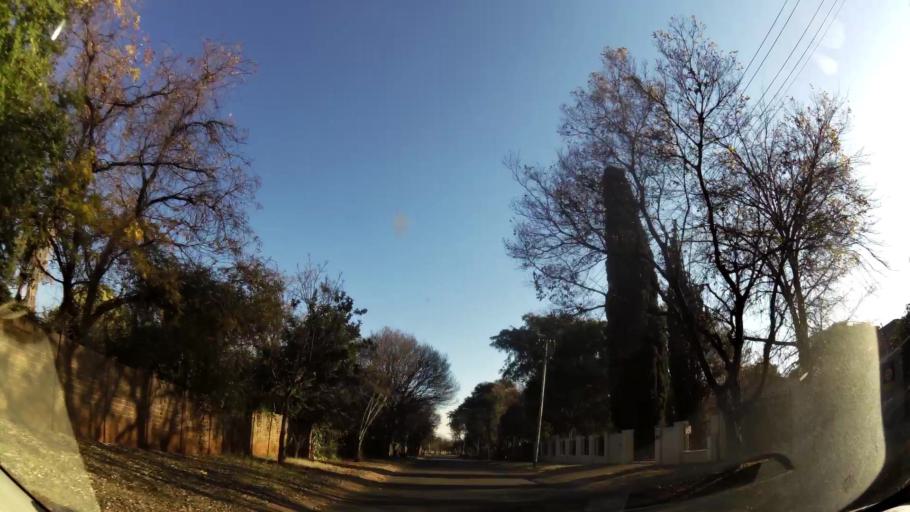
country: ZA
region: Gauteng
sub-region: City of Tshwane Metropolitan Municipality
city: Centurion
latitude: -25.8554
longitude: 28.1496
